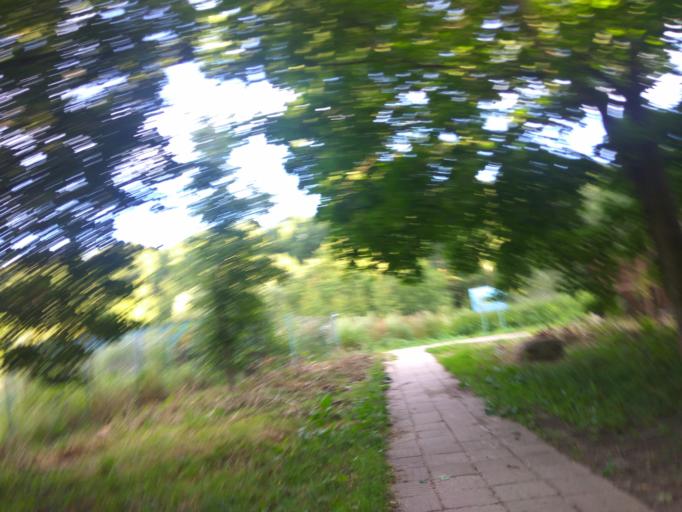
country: RU
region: Moscow
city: Chertanovo Yuzhnoye
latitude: 55.6051
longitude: 37.5778
